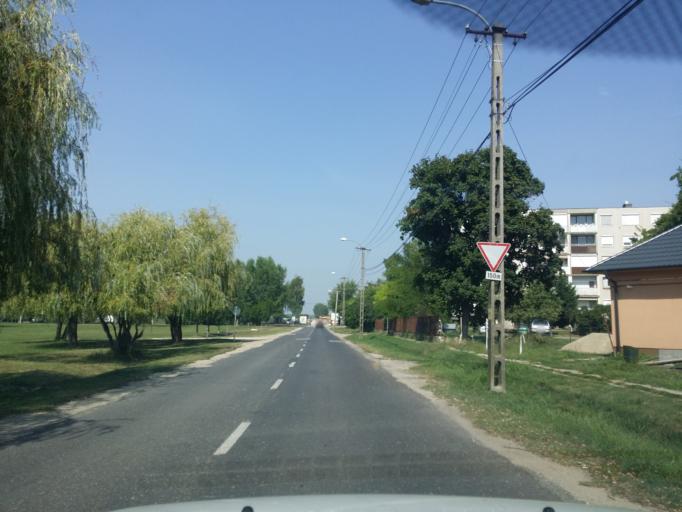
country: HU
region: Fejer
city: Sarbogard
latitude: 46.8903
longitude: 18.6255
